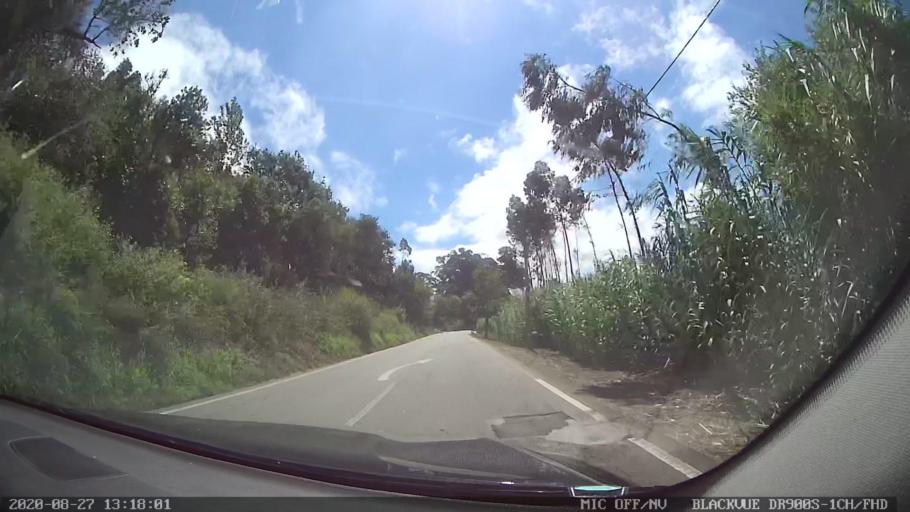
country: PT
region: Aveiro
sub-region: Vagos
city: Vagos
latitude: 40.5773
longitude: -8.6795
